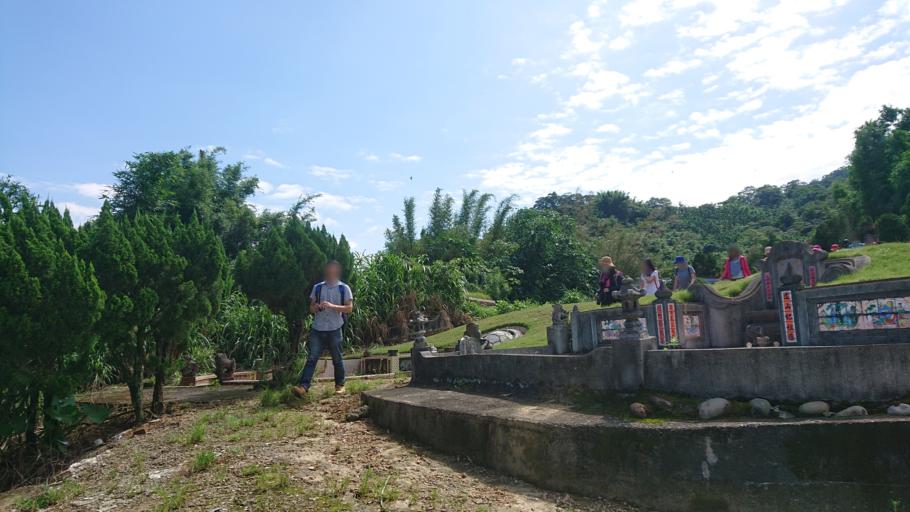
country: TW
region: Taiwan
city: Daxi
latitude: 24.8998
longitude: 121.3769
